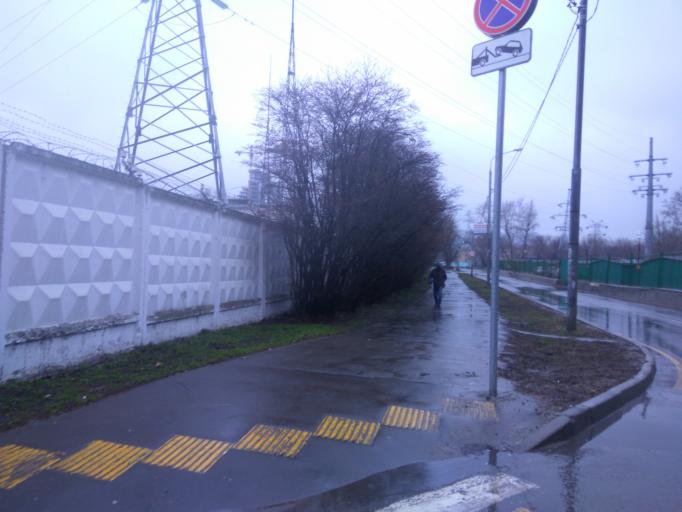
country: RU
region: Moscow
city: Vorob'yovo
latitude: 55.7431
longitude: 37.5184
